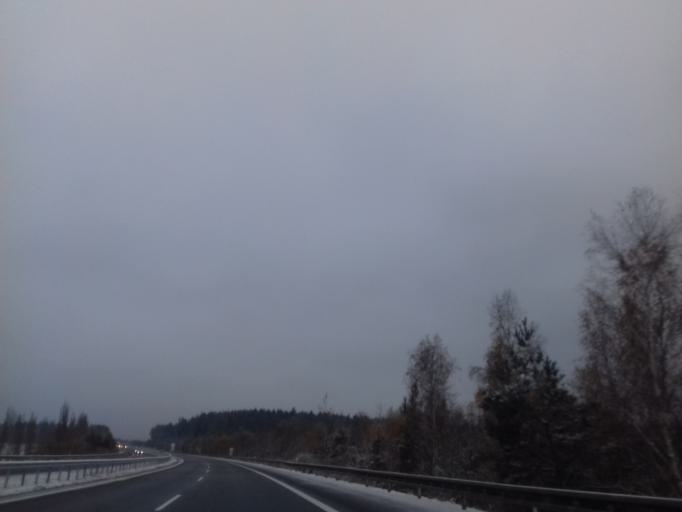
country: CZ
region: Plzensky
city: Myto
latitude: 49.8150
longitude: 13.7610
